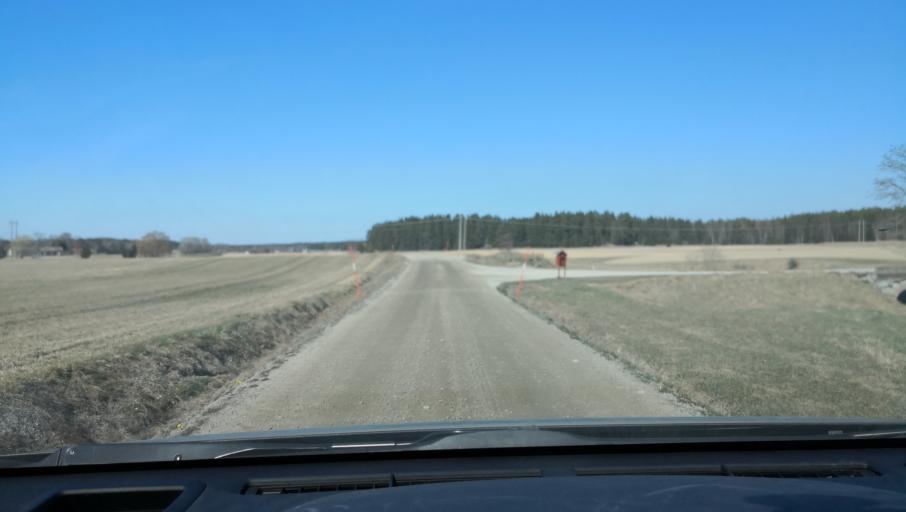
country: SE
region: Vaestmanland
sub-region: Sala Kommun
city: Sala
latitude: 59.8933
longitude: 16.5303
